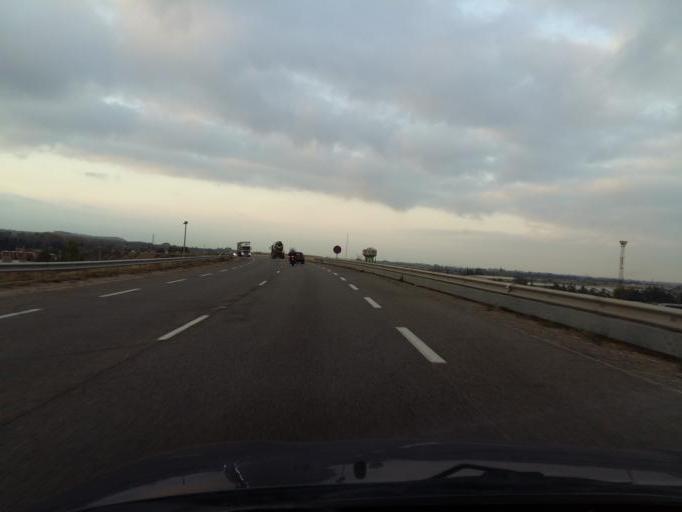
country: FR
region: Provence-Alpes-Cote d'Azur
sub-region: Departement des Bouches-du-Rhone
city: Miramas
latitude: 43.5828
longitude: 4.9855
